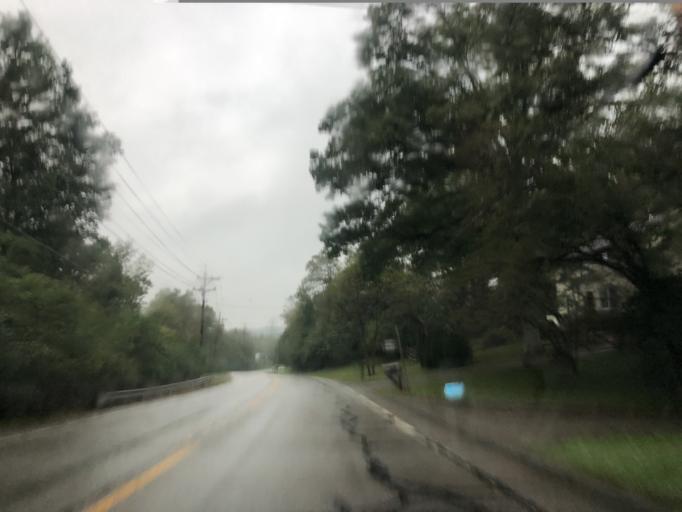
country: US
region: Ohio
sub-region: Hamilton County
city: The Village of Indian Hill
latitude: 39.2312
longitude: -84.3139
